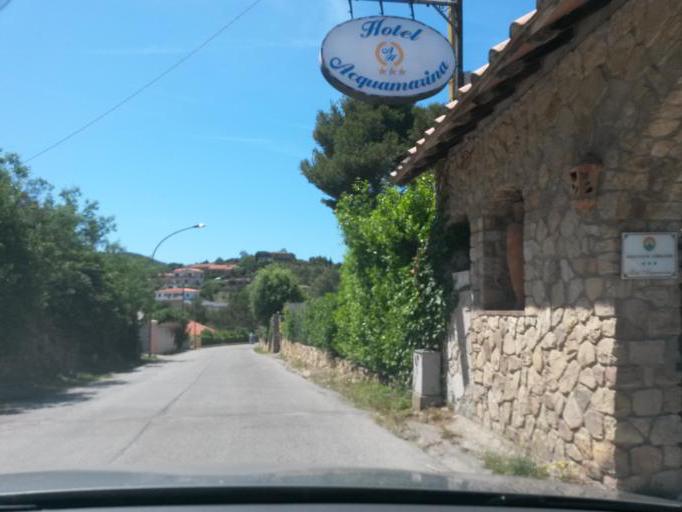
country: IT
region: Tuscany
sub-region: Provincia di Livorno
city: Portoferraio
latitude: 42.8177
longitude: 10.3161
